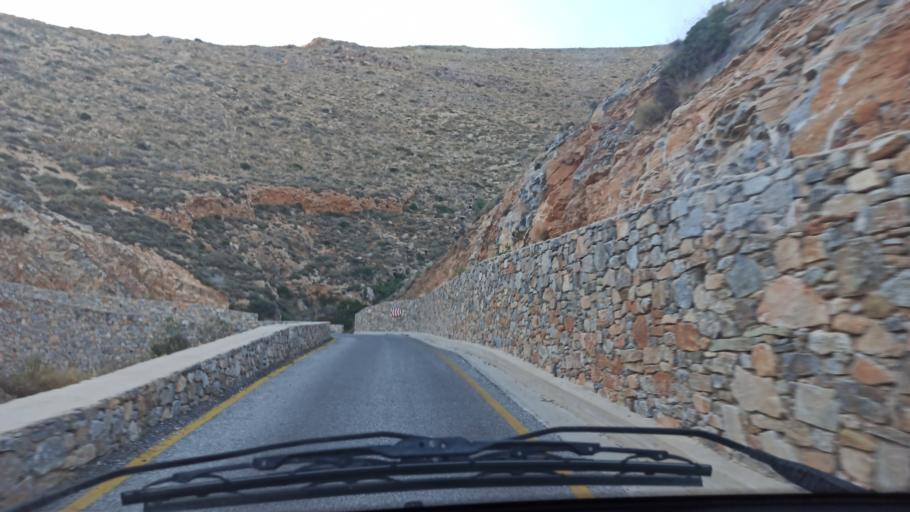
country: GR
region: South Aegean
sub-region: Nomos Kykladon
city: Ano Syros
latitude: 37.4546
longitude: 24.9352
